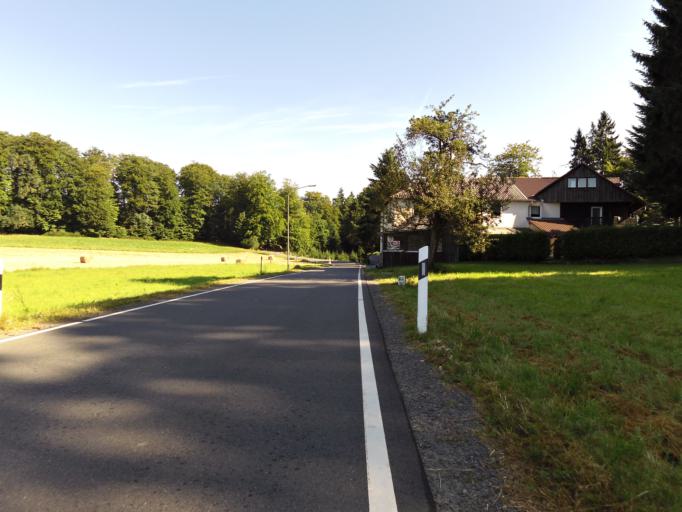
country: DE
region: Hesse
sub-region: Regierungsbezirk Darmstadt
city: Lindenfels
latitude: 49.6963
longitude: 8.7218
